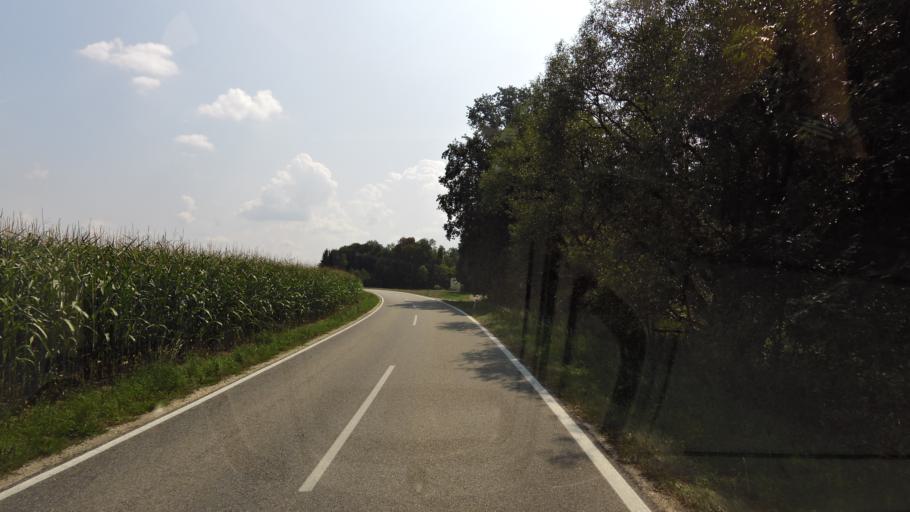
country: AT
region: Upper Austria
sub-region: Politischer Bezirk Ried im Innkreis
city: Waldzell
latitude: 48.1827
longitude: 13.3968
